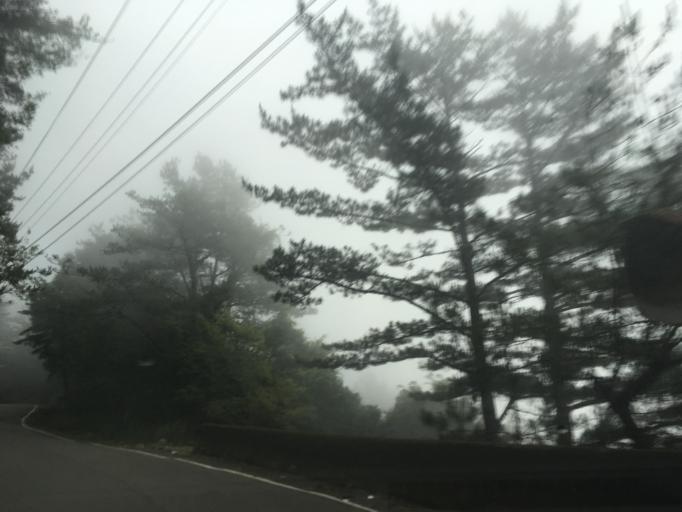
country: TW
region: Taiwan
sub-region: Nantou
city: Puli
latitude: 24.2573
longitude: 121.0116
